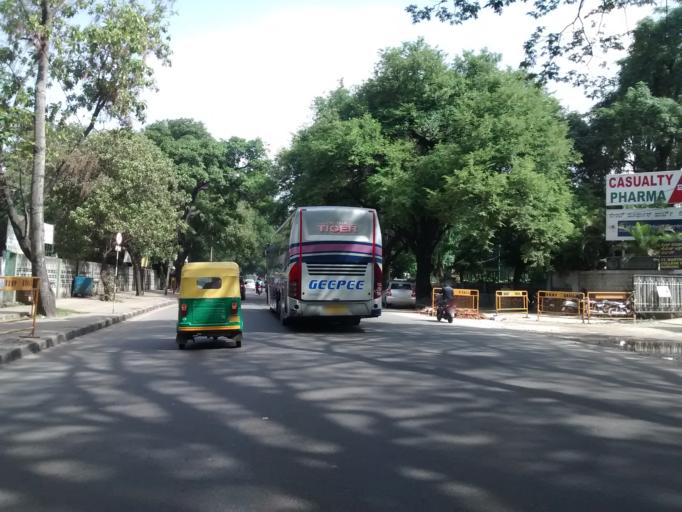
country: IN
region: Karnataka
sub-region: Bangalore Urban
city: Bangalore
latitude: 12.9714
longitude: 77.5869
